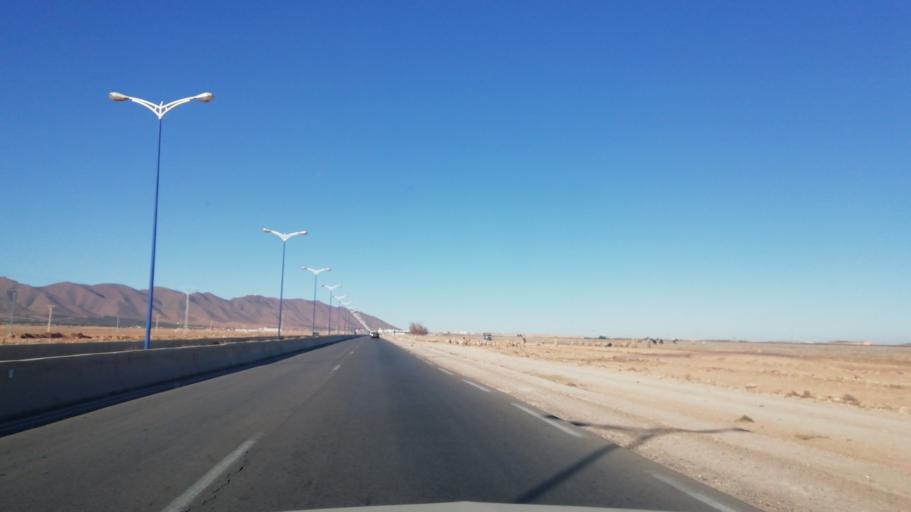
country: DZ
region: Wilaya de Naama
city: Naama
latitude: 33.4926
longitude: -0.2891
